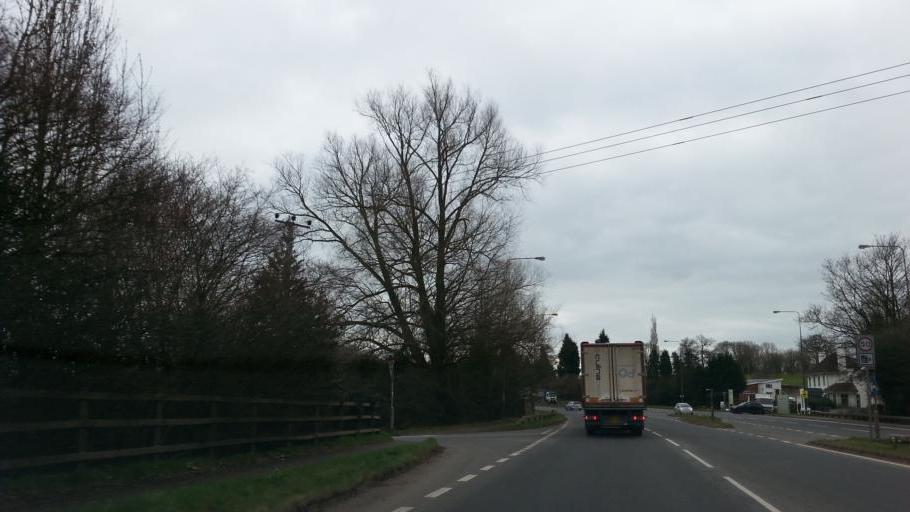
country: GB
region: England
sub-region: Staffordshire
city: Stone
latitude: 52.9048
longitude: -2.1612
